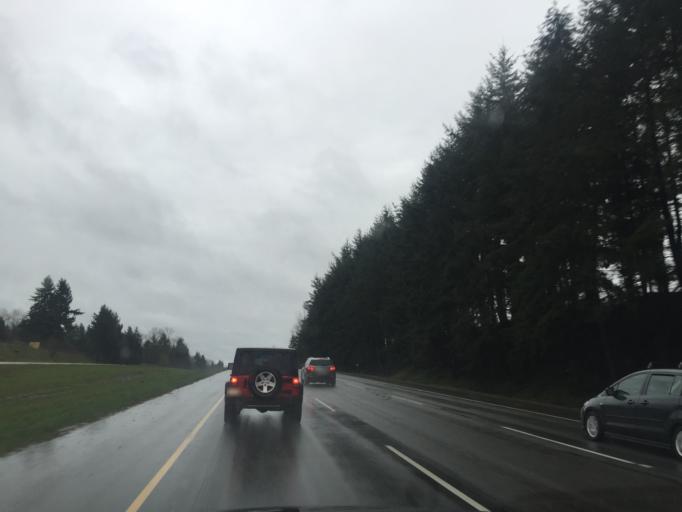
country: CA
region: British Columbia
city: Langley
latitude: 49.1184
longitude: -122.5360
